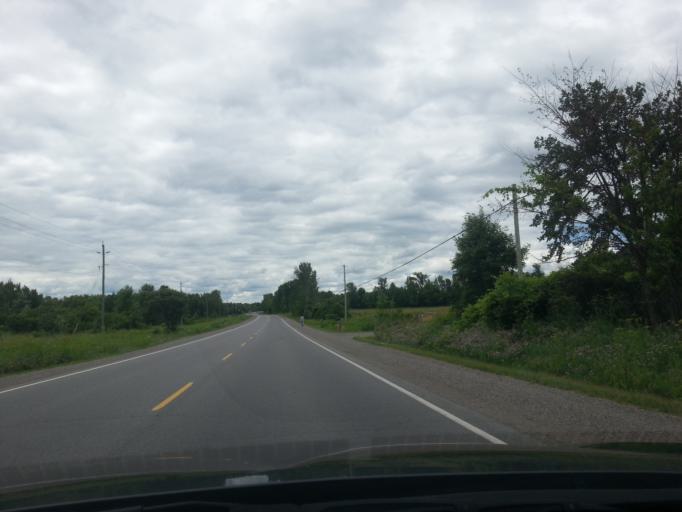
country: CA
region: Ontario
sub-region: Lanark County
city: Smiths Falls
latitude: 44.8592
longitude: -76.0532
